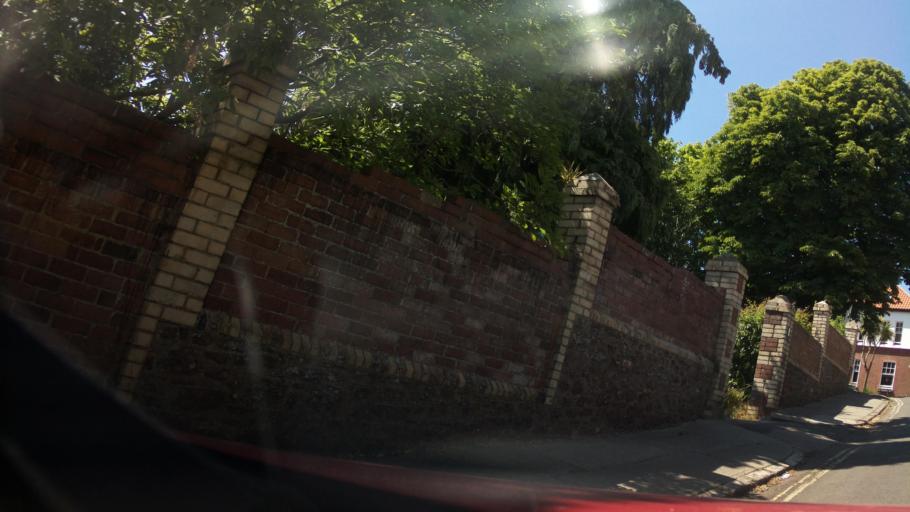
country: GB
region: England
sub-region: Borough of Torbay
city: Paignton
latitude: 50.4290
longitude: -3.5621
